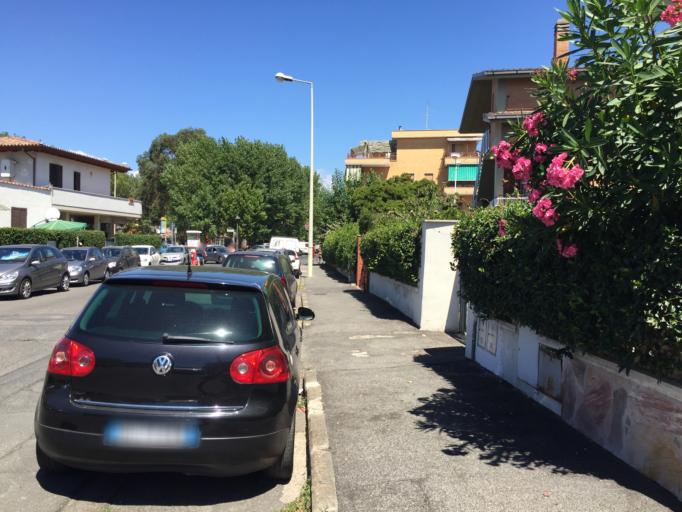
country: IT
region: Latium
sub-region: Citta metropolitana di Roma Capitale
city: Ladispoli
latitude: 41.9535
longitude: 12.0656
